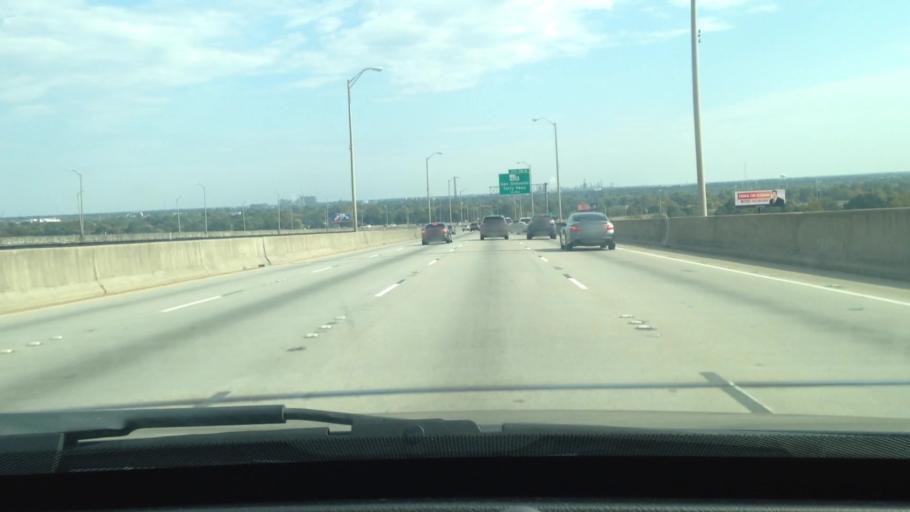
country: US
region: Louisiana
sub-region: Jefferson Parish
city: Gretna
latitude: 29.9379
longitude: -90.0483
